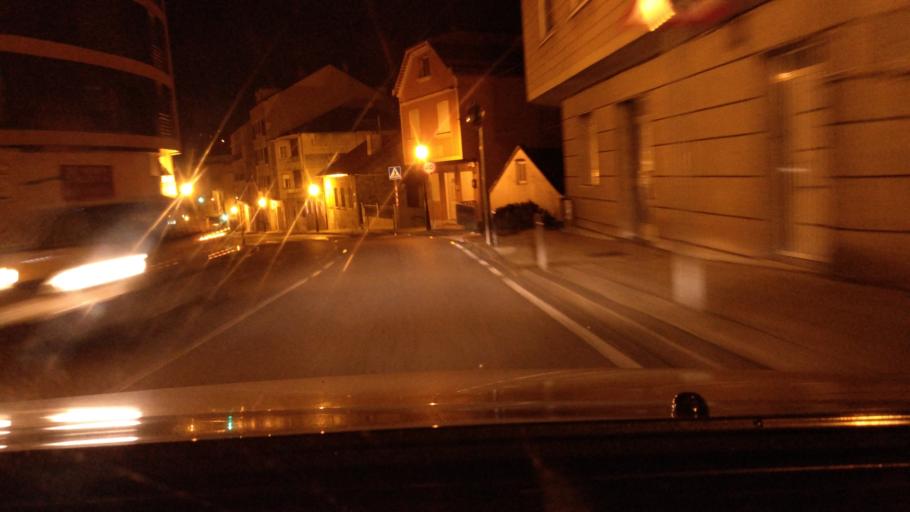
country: ES
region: Galicia
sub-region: Provincia de Pontevedra
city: Moana
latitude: 42.2782
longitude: -8.7373
